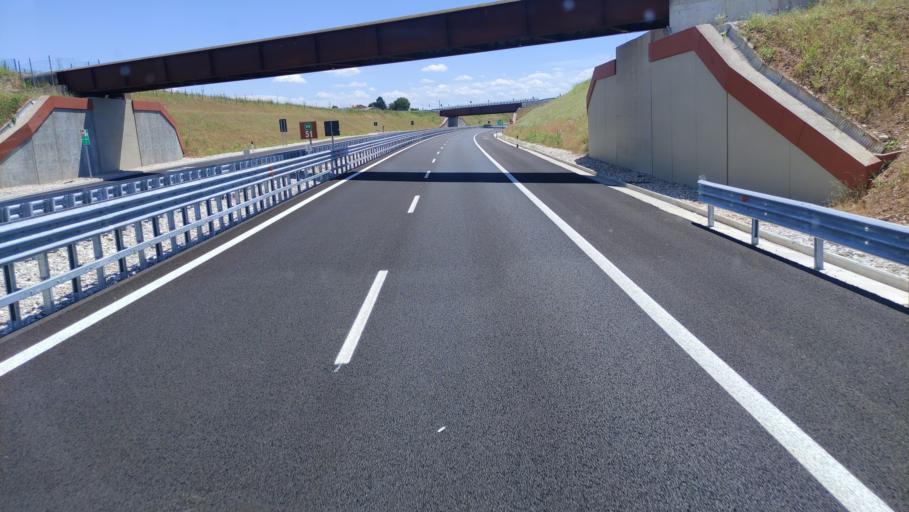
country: IT
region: Veneto
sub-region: Provincia di Treviso
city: Altivole
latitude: 45.7400
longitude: 11.9436
